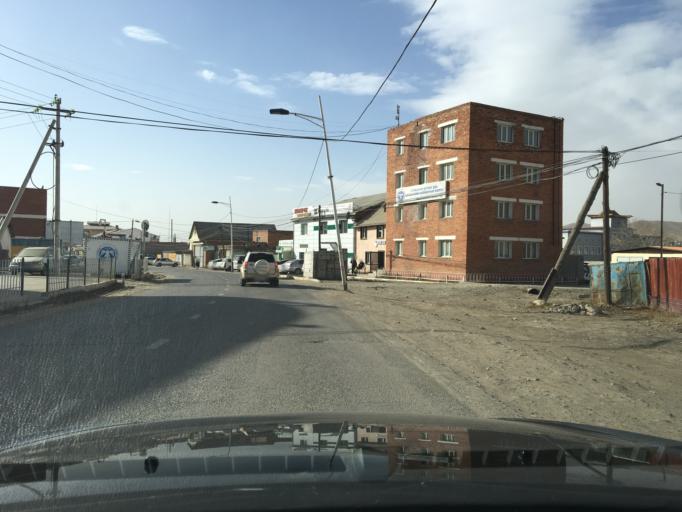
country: MN
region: Ulaanbaatar
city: Ulaanbaatar
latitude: 47.9825
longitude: 106.9398
